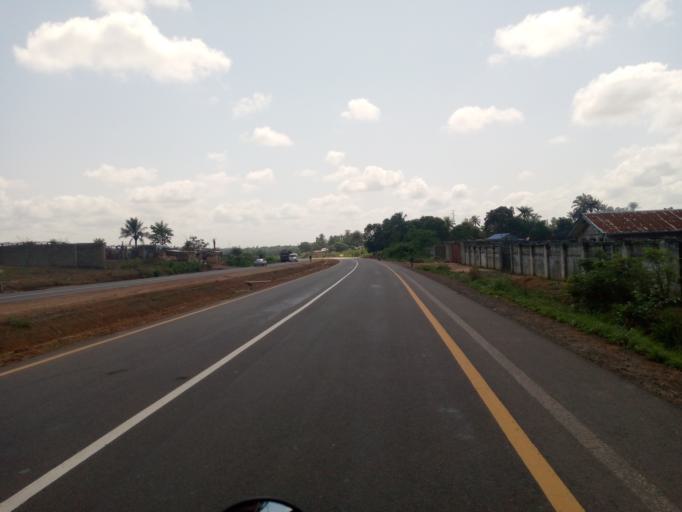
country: SL
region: Western Area
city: Waterloo
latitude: 8.3625
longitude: -12.9650
